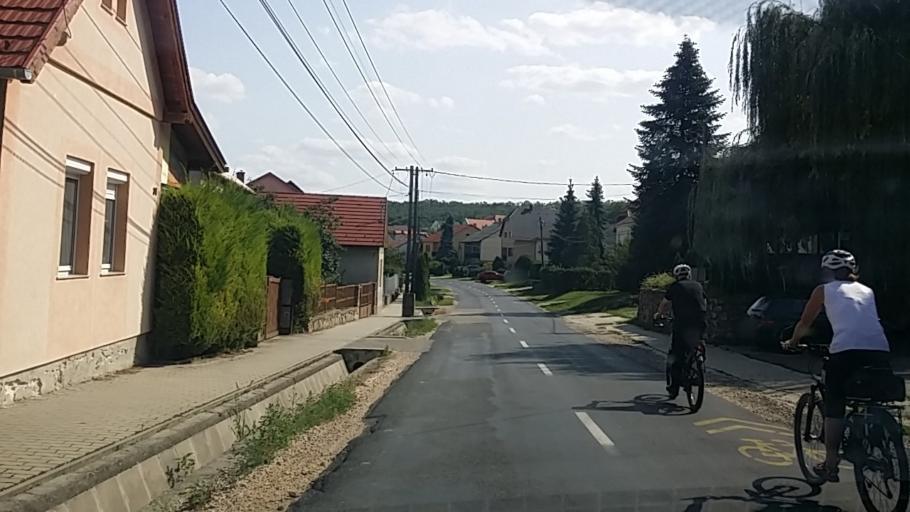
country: HU
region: Gyor-Moson-Sopron
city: Nagycenk
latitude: 47.6467
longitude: 16.6675
